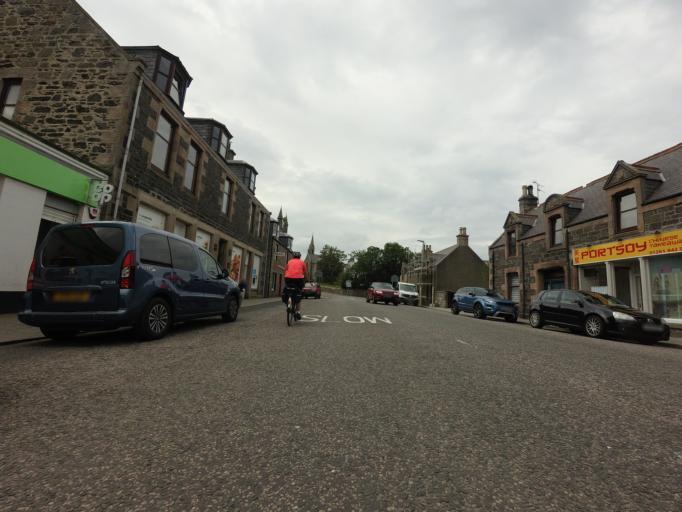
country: GB
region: Scotland
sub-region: Aberdeenshire
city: Portsoy
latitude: 57.6814
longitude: -2.6915
